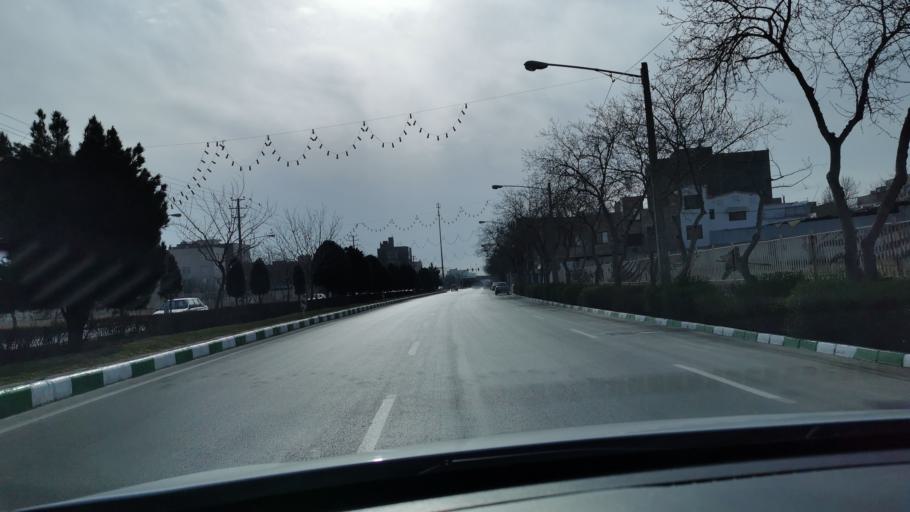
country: IR
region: Razavi Khorasan
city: Mashhad
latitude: 36.2998
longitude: 59.5227
